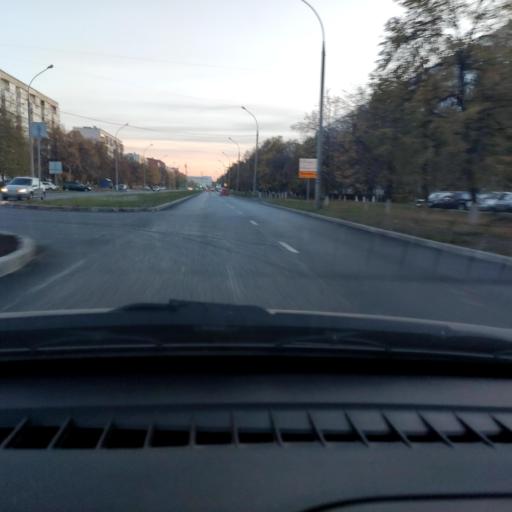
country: RU
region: Samara
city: Tol'yatti
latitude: 53.5377
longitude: 49.3296
